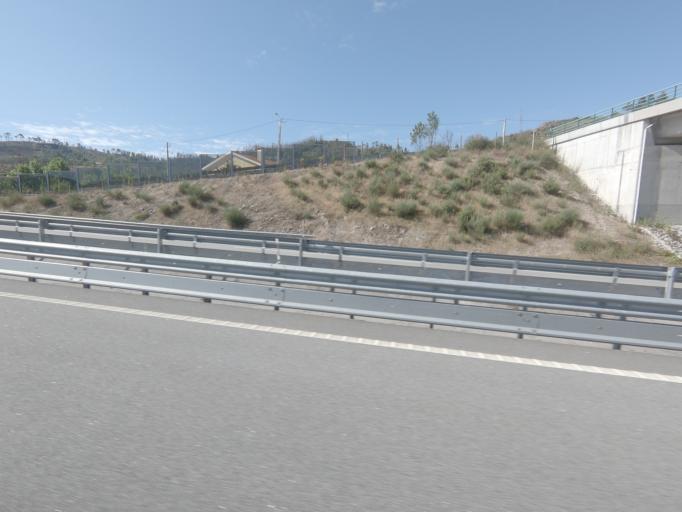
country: PT
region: Porto
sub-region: Amarante
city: Amarante
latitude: 41.2618
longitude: -8.0084
